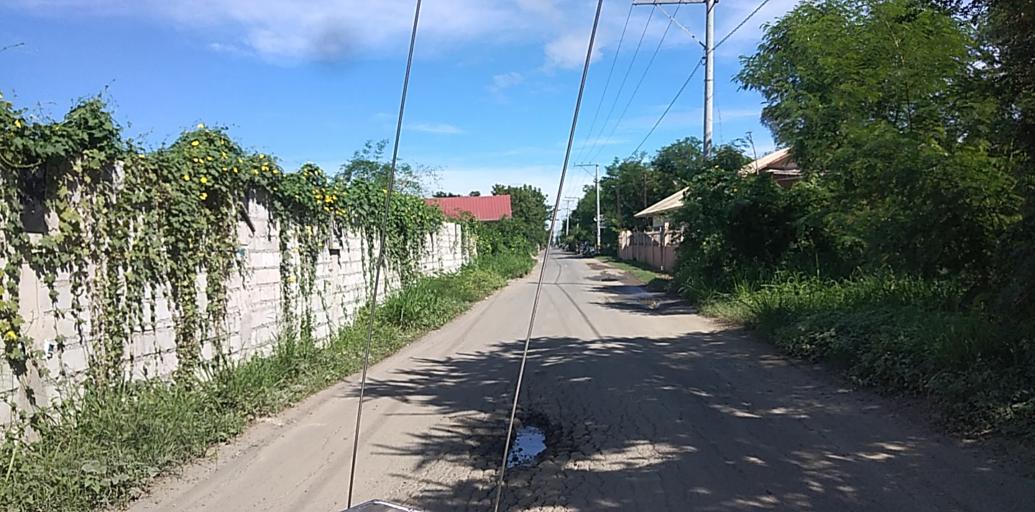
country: PH
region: Central Luzon
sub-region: Province of Pampanga
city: Candaba
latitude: 15.0778
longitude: 120.8080
